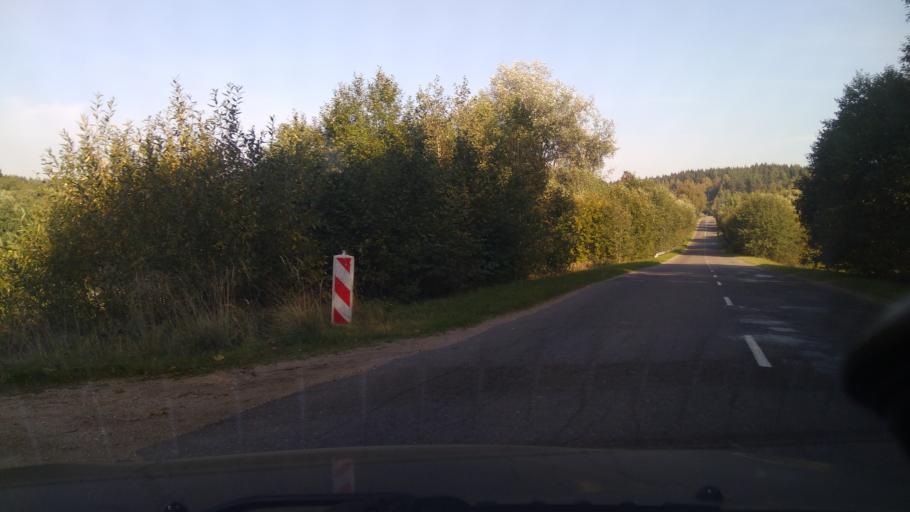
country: BY
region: Minsk
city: Rakaw
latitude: 54.0247
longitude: 27.0539
